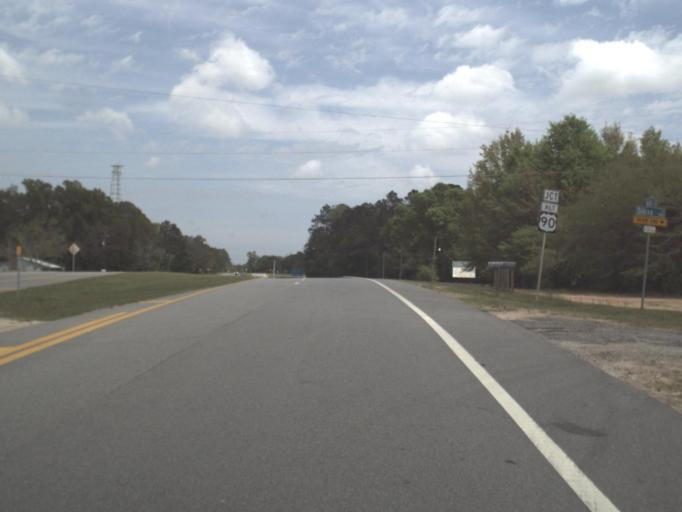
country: US
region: Florida
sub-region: Escambia County
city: Cantonment
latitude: 30.5345
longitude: -87.4149
